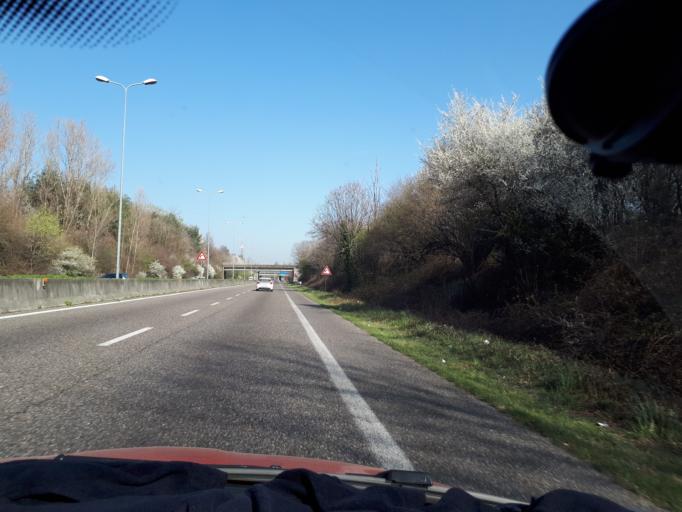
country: IT
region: Lombardy
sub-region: Provincia di Monza e Brianza
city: Seveso
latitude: 45.6470
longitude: 9.1553
